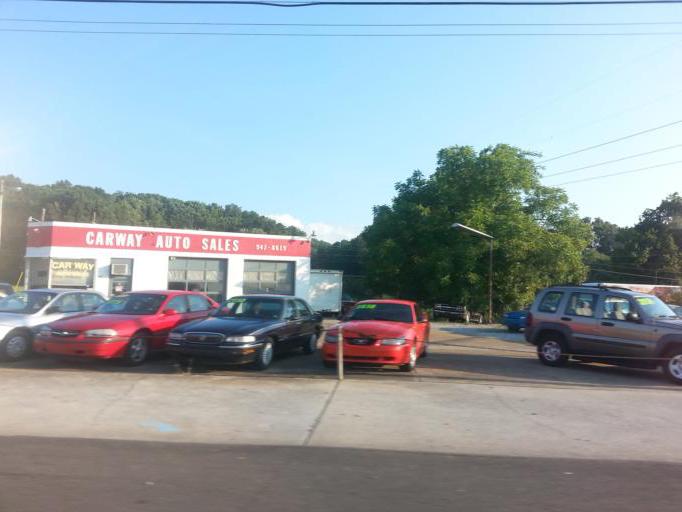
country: US
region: Tennessee
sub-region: Knox County
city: Knoxville
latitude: 36.0144
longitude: -84.0362
